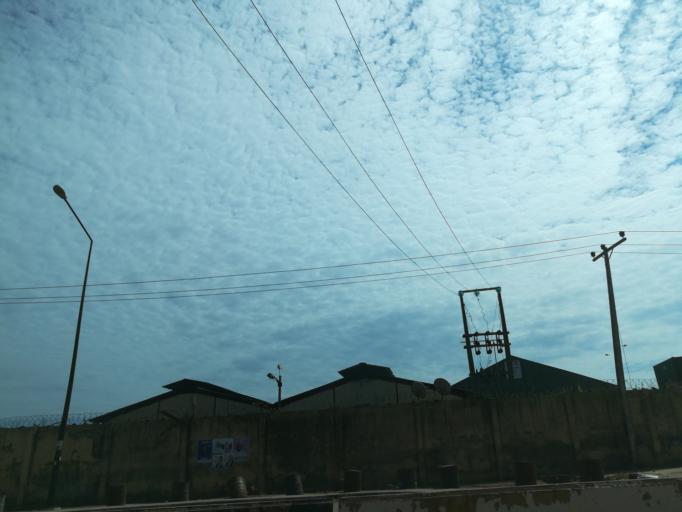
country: NG
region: Lagos
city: Ebute Ikorodu
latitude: 6.5937
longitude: 3.5061
